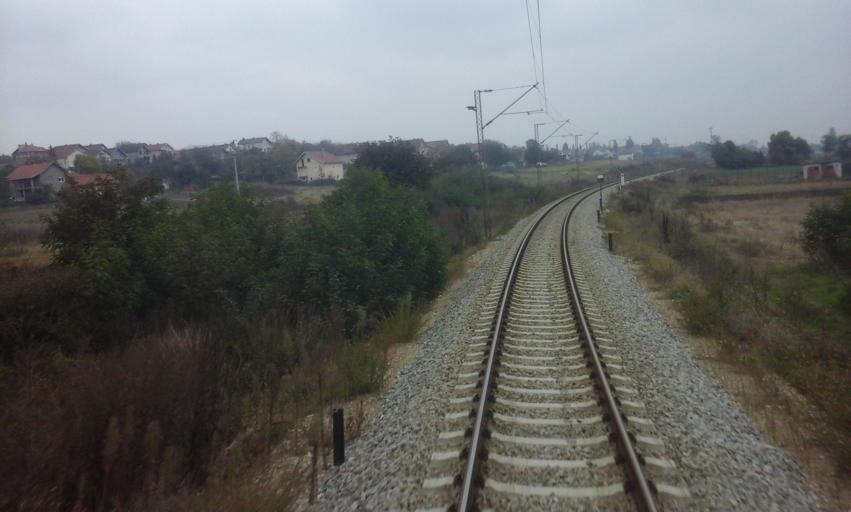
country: RS
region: Central Serbia
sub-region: Belgrade
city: Mladenovac
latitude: 44.4573
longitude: 20.6729
